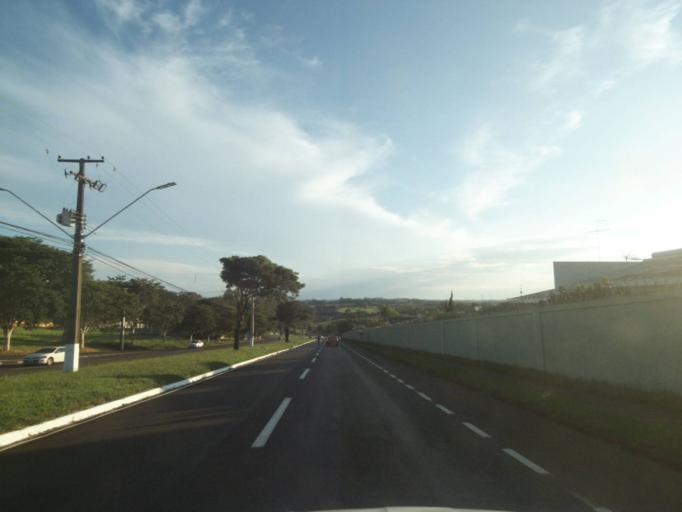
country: BR
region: Parana
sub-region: Londrina
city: Londrina
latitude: -23.3479
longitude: -51.1904
